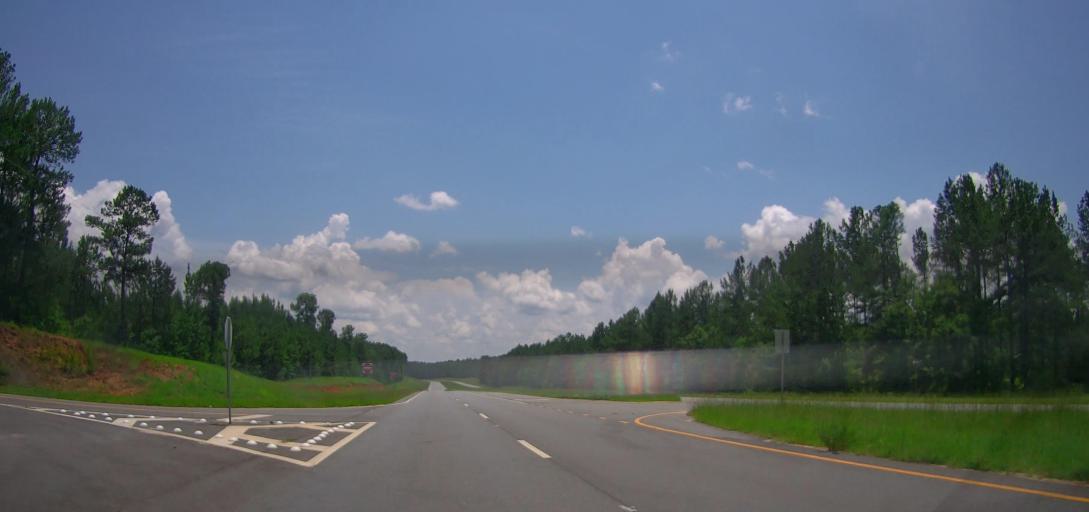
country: US
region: Georgia
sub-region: Upson County
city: Thomaston
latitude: 32.8041
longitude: -84.2764
